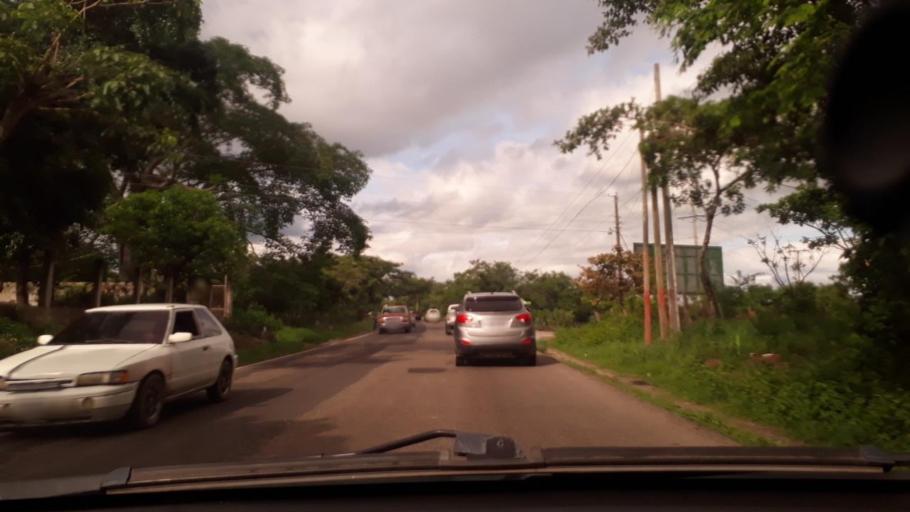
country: GT
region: Jutiapa
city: Quesada
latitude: 14.2751
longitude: -89.9718
